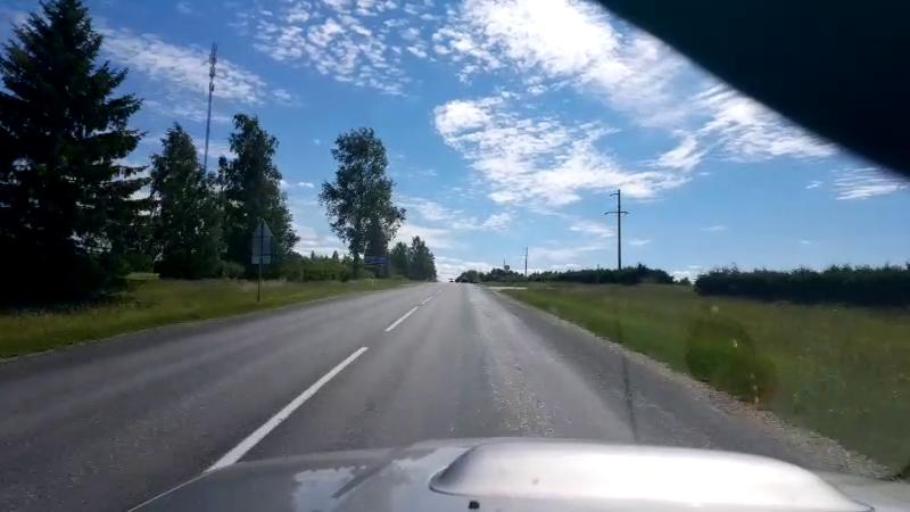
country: EE
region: Laeaene-Virumaa
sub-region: Rakke vald
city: Rakke
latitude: 58.8513
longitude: 26.2916
